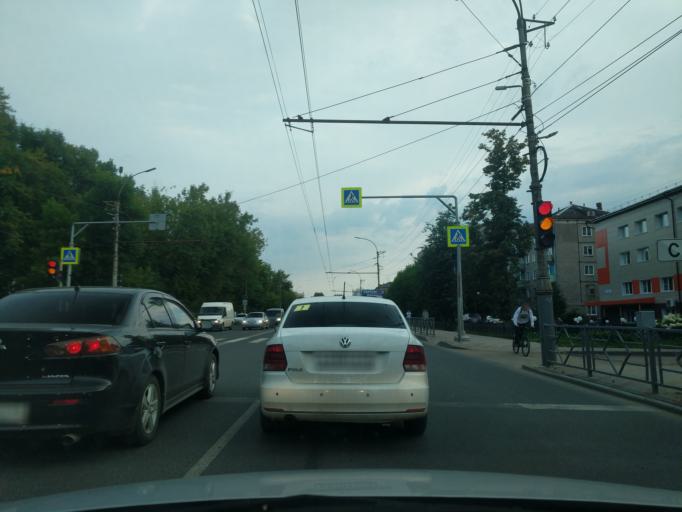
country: RU
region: Kirov
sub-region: Kirovo-Chepetskiy Rayon
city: Kirov
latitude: 58.6174
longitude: 49.6563
